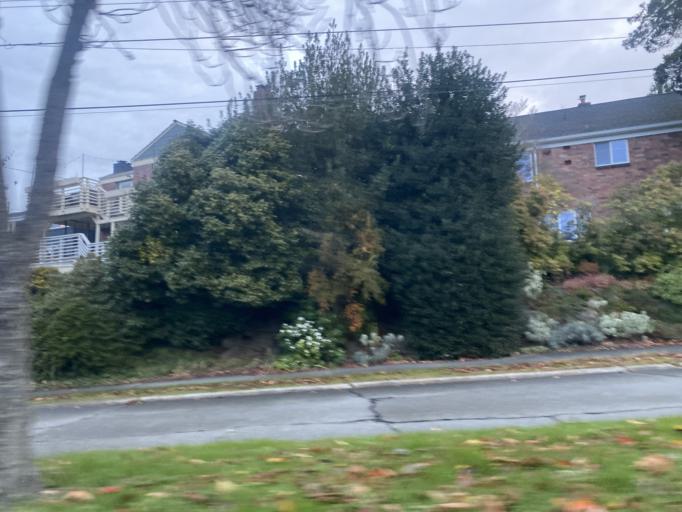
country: US
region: Washington
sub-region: King County
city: Seattle
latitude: 47.6387
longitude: -122.3964
